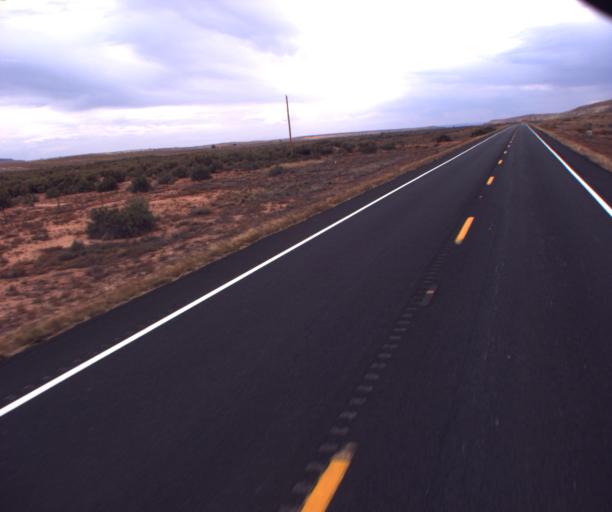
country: US
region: Arizona
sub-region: Coconino County
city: Kaibito
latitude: 36.3514
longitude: -110.9096
